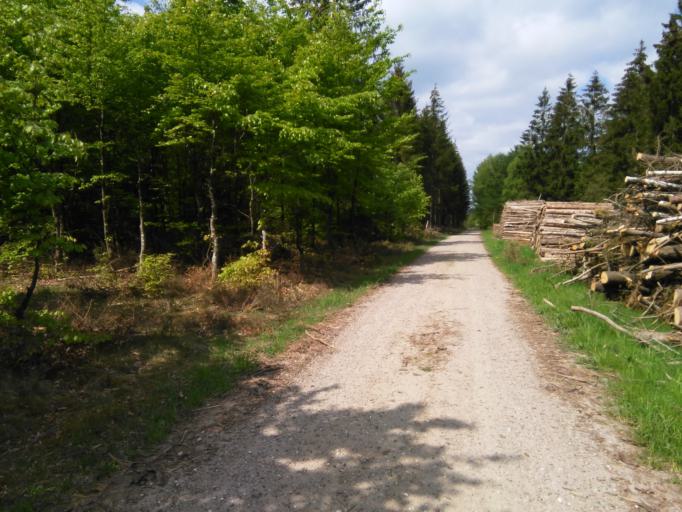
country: DK
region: Central Jutland
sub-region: Silkeborg Kommune
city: Svejbaek
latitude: 56.0573
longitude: 9.6552
